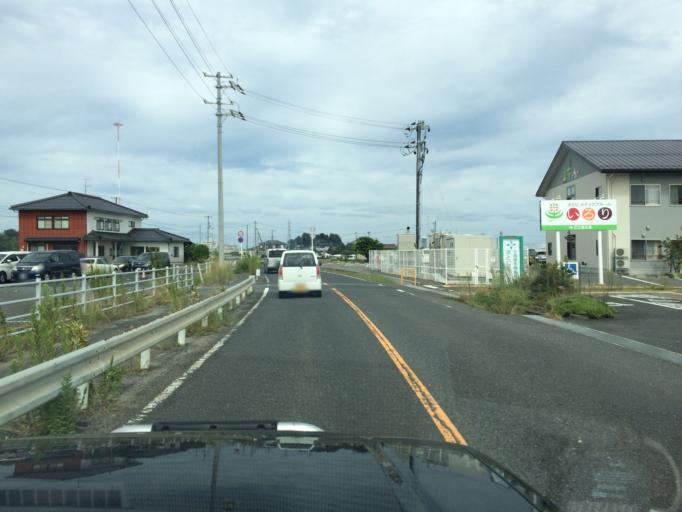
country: JP
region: Tottori
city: Tottori
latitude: 35.5031
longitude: 134.1934
